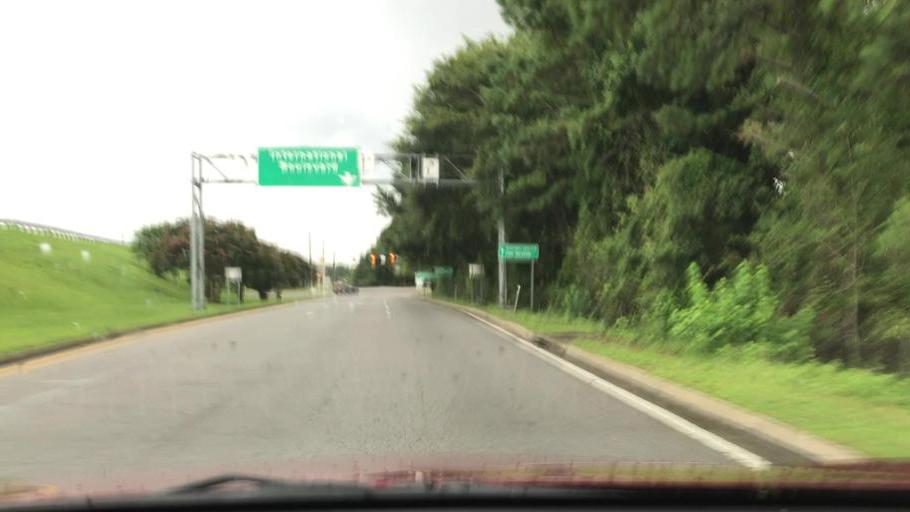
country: US
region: South Carolina
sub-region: Charleston County
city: North Charleston
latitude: 32.8618
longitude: -80.0249
